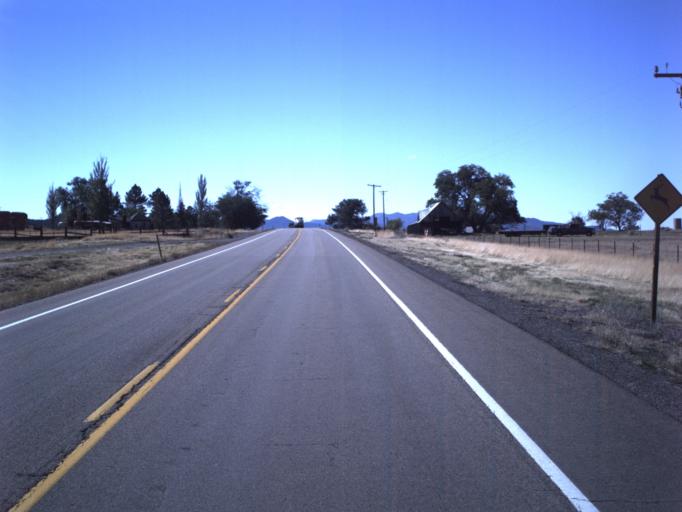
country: US
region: Utah
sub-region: Juab County
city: Nephi
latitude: 39.4450
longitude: -111.9131
